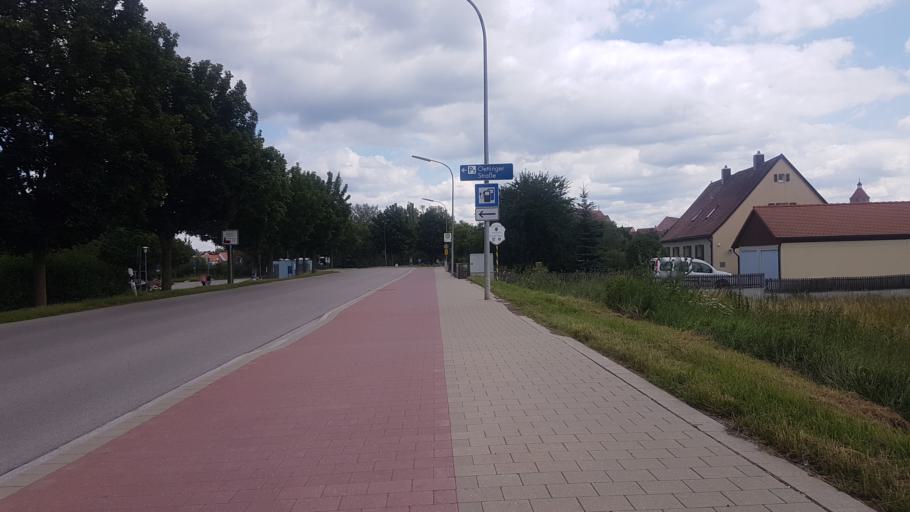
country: DE
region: Bavaria
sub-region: Regierungsbezirk Mittelfranken
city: Gunzenhausen
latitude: 49.1142
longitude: 10.7494
